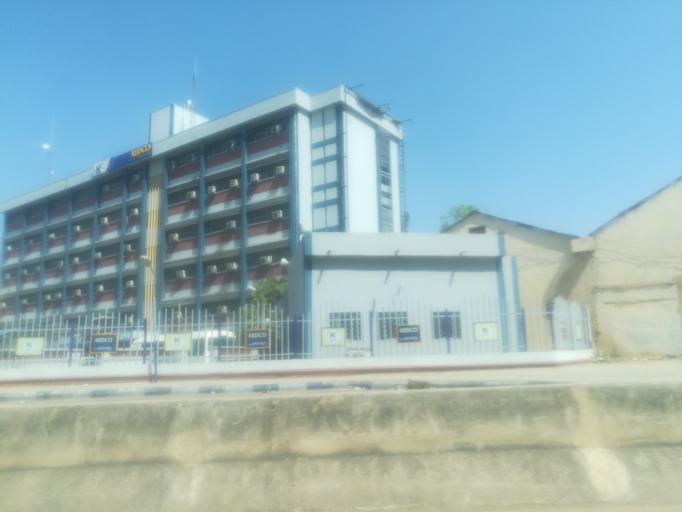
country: NG
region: Kano
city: Kano
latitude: 12.0035
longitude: 8.5370
